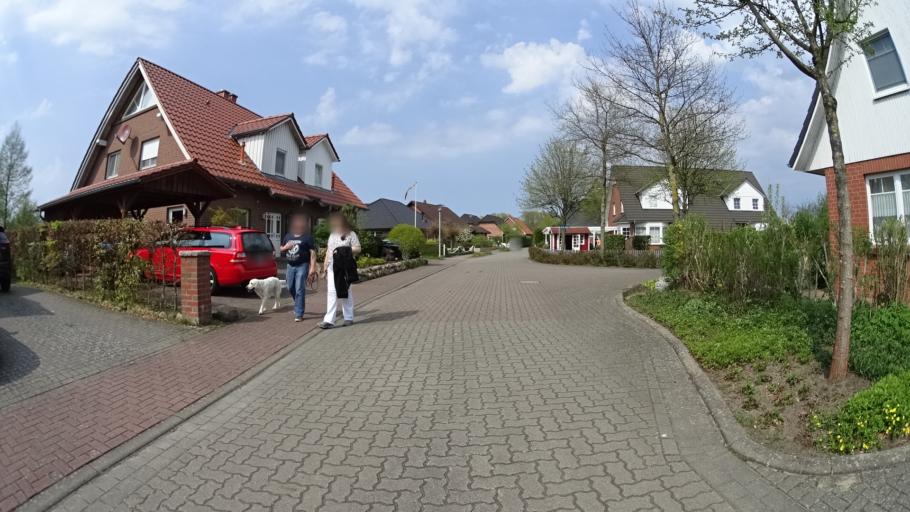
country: DE
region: Lower Saxony
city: Jork
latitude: 53.5382
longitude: 9.6925
